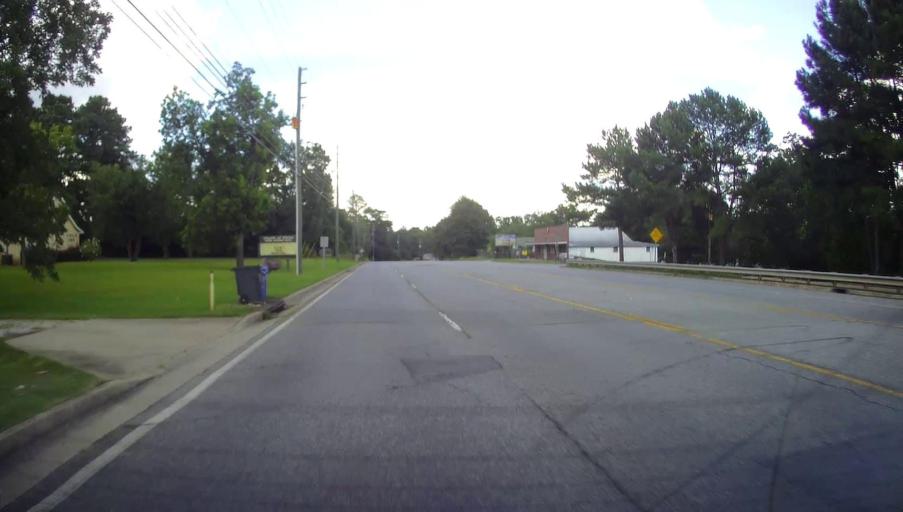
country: US
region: Georgia
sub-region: Muscogee County
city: Columbus
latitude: 32.5267
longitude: -84.9138
